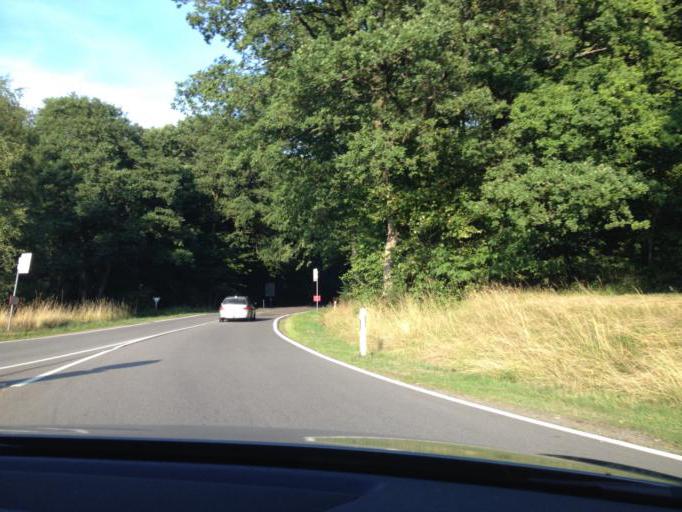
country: DE
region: Saarland
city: Tholey
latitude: 49.5321
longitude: 7.0405
